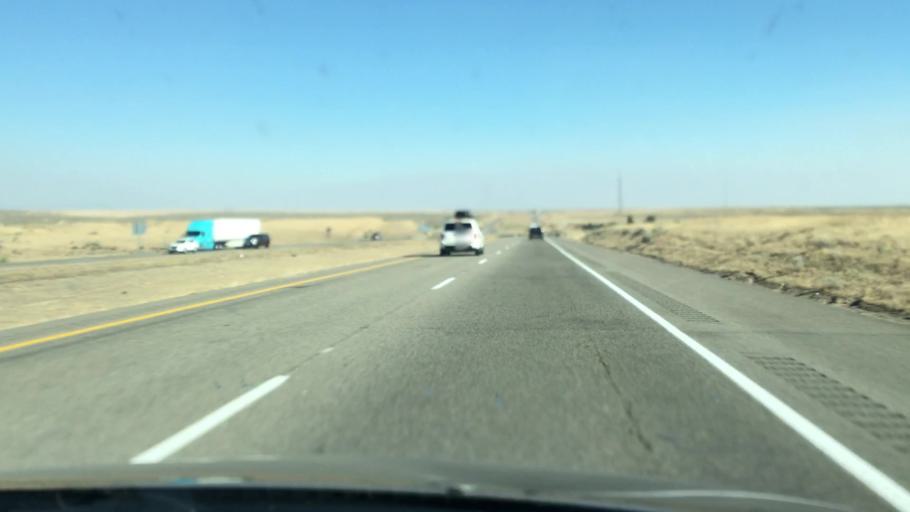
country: US
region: Idaho
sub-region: Ada County
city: Boise
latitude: 43.4653
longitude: -116.0946
